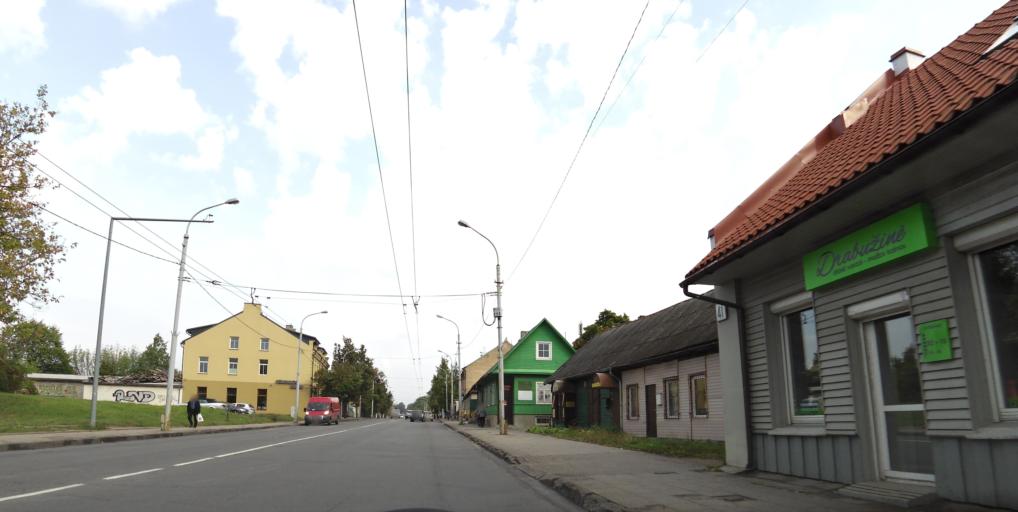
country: LT
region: Vilnius County
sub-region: Vilnius
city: Vilnius
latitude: 54.6972
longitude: 25.2820
